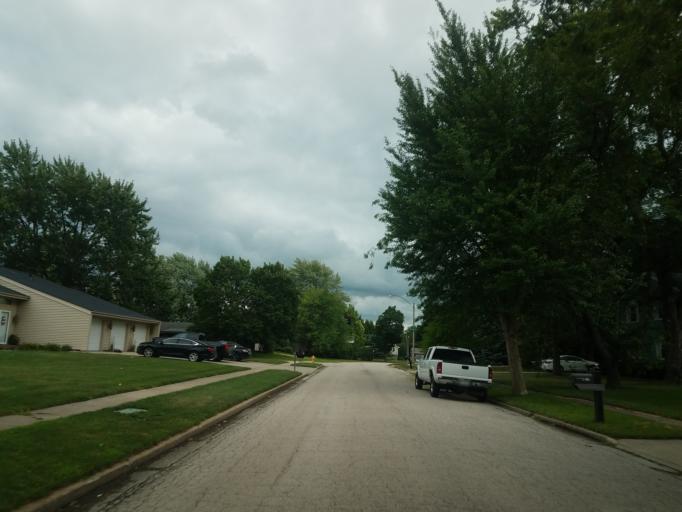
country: US
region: Illinois
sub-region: McLean County
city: Bloomington
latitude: 40.4777
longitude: -88.9462
